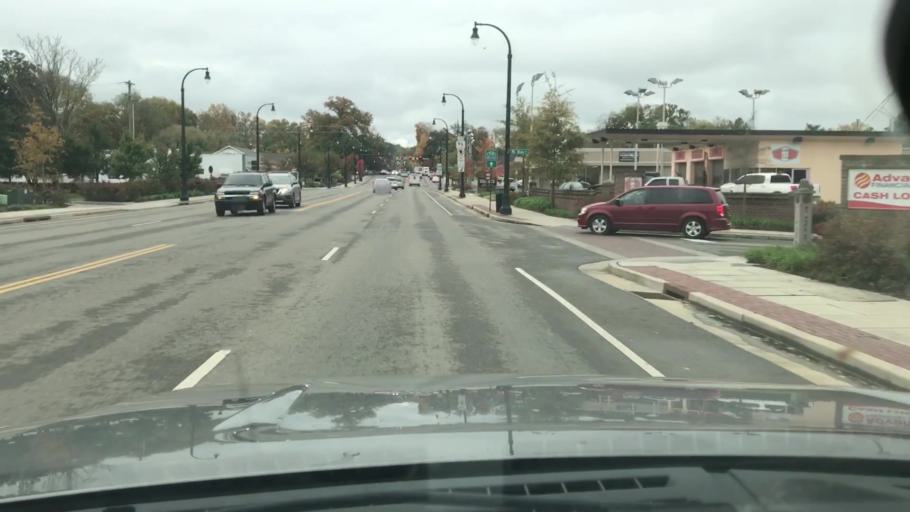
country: US
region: Tennessee
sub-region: Williamson County
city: Franklin
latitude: 35.9277
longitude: -86.8744
